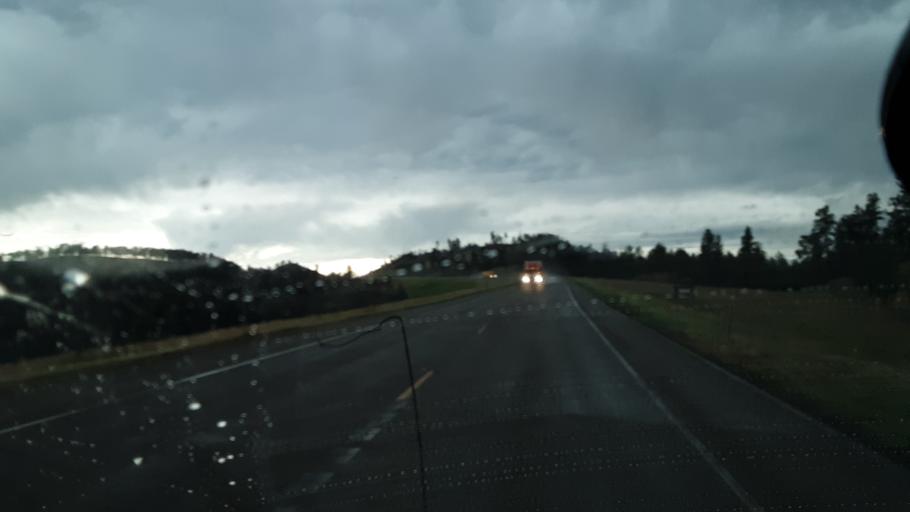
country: US
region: Montana
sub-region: Powder River County
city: Broadus
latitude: 45.5512
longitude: -105.8787
